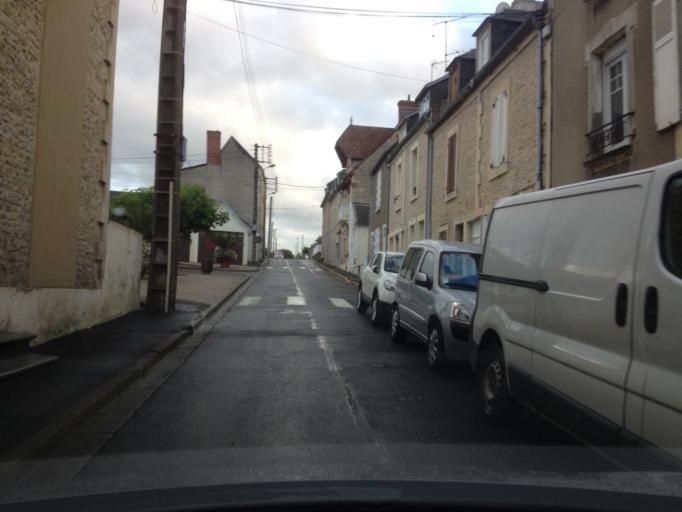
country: FR
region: Lower Normandy
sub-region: Departement du Calvados
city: Grandcamp-Maisy
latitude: 49.3881
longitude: -1.0415
